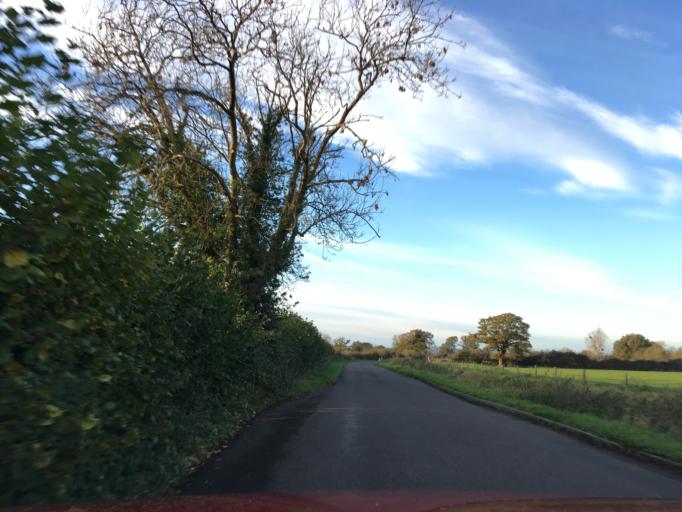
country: GB
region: England
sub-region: South Gloucestershire
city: Hill
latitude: 51.6400
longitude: -2.5061
